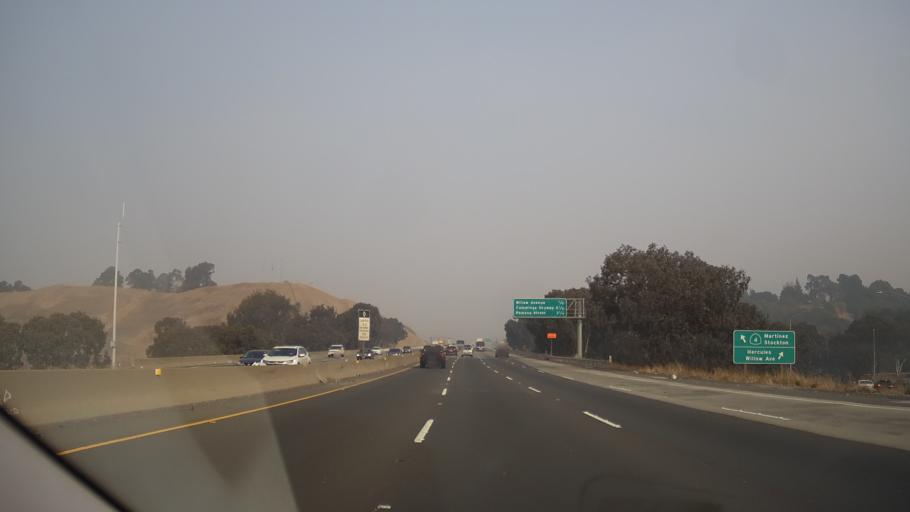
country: US
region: California
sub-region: Contra Costa County
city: Hercules
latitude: 38.0134
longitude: -122.2699
